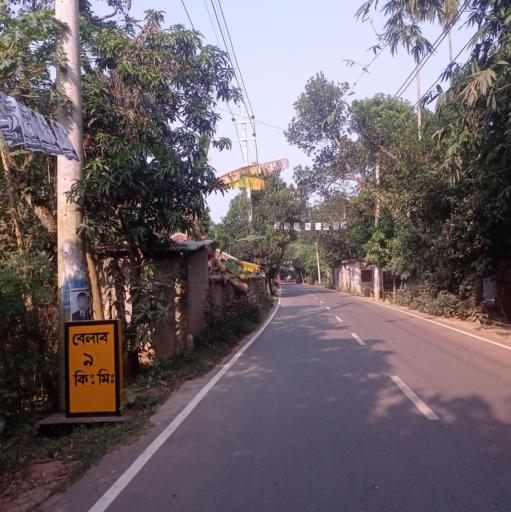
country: BD
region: Dhaka
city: Bhairab Bazar
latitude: 24.0427
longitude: 90.8340
